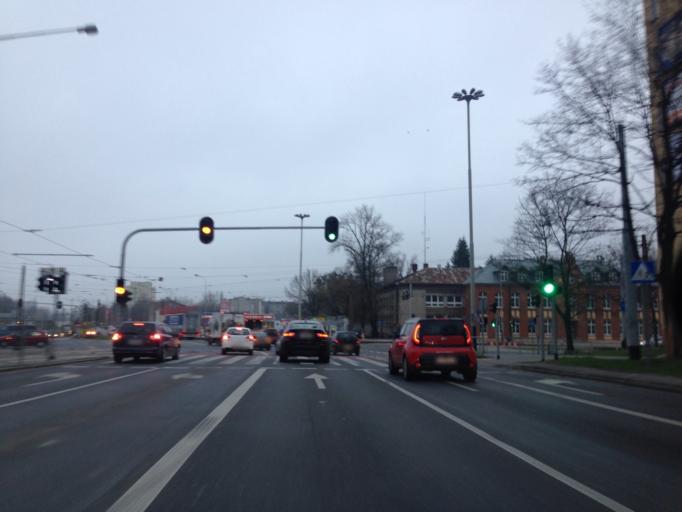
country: PL
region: Lodz Voivodeship
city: Lodz
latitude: 51.7622
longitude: 19.4847
